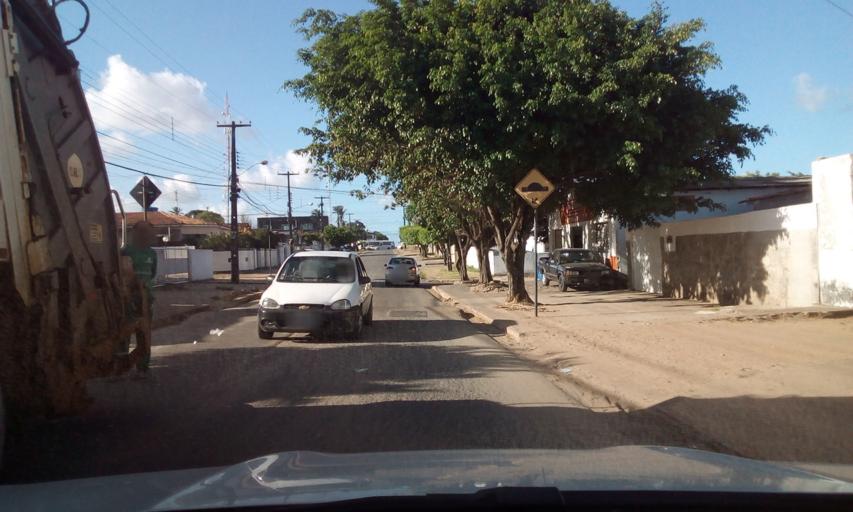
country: BR
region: Paraiba
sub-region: Bayeux
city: Bayeux
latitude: -7.1378
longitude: -34.9118
